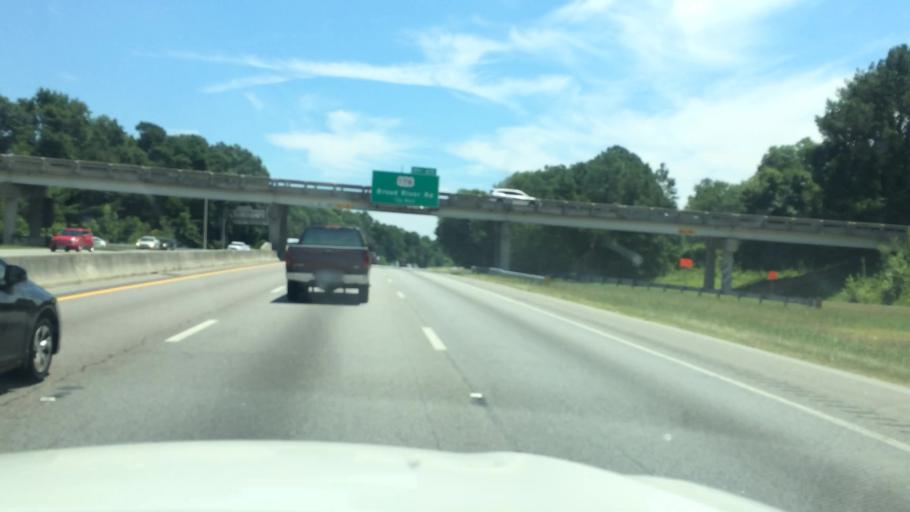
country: US
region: South Carolina
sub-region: Lexington County
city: Saint Andrews
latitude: 34.0374
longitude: -81.1081
